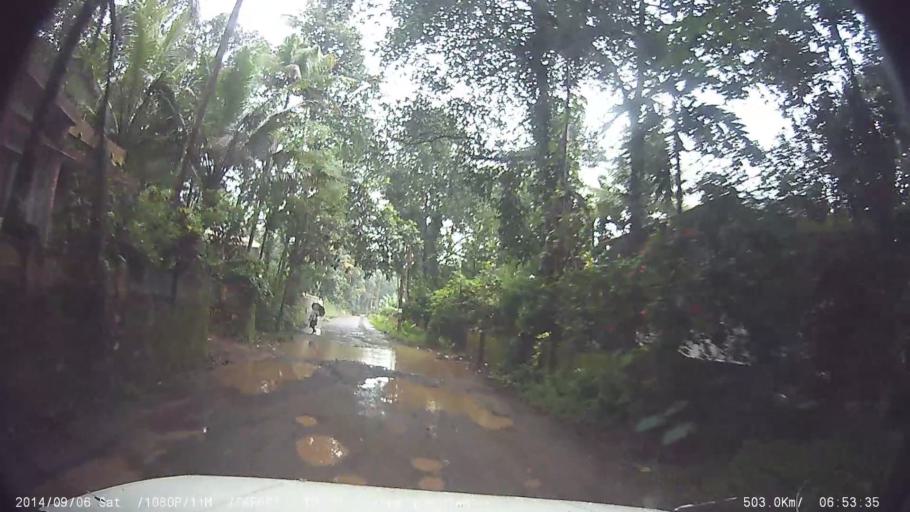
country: IN
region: Kerala
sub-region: Ernakulam
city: Piravam
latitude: 9.7875
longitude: 76.5217
